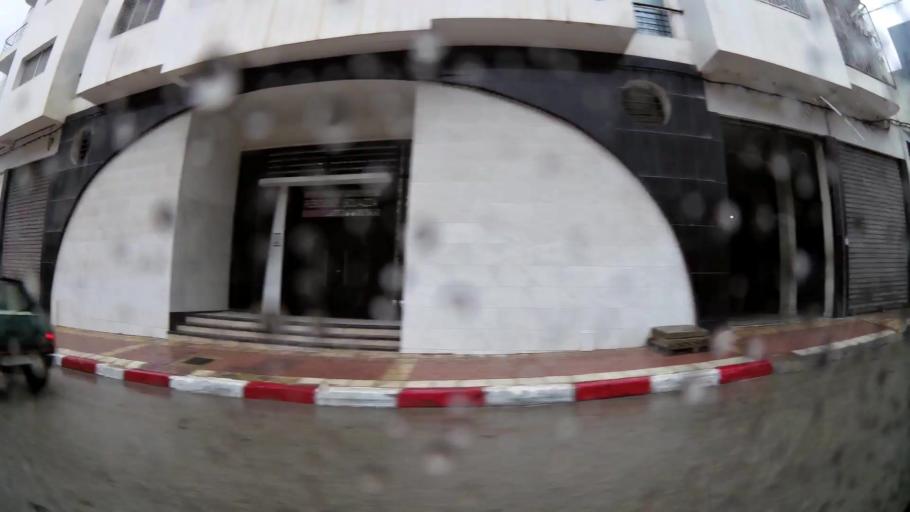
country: MA
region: Taza-Al Hoceima-Taounate
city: Al Hoceima
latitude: 35.2518
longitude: -3.9412
